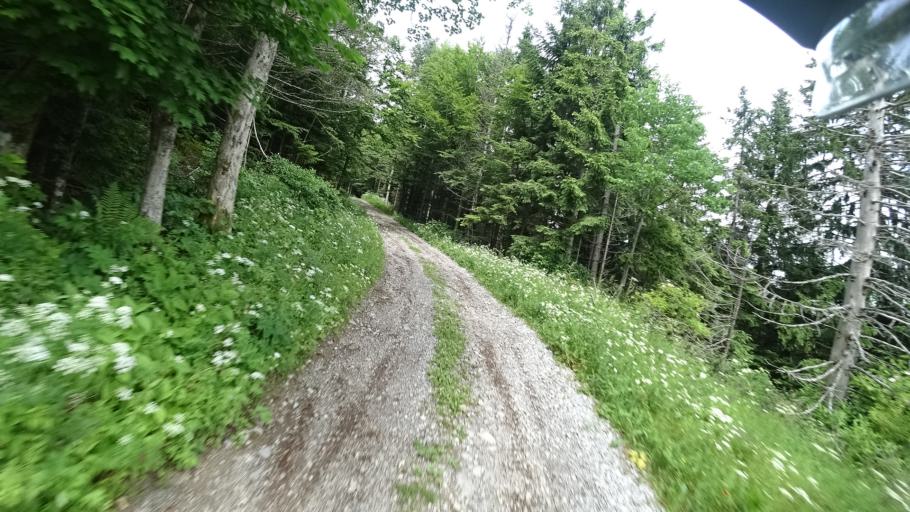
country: HR
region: Primorsko-Goranska
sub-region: Grad Delnice
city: Delnice
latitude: 45.3329
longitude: 14.7765
